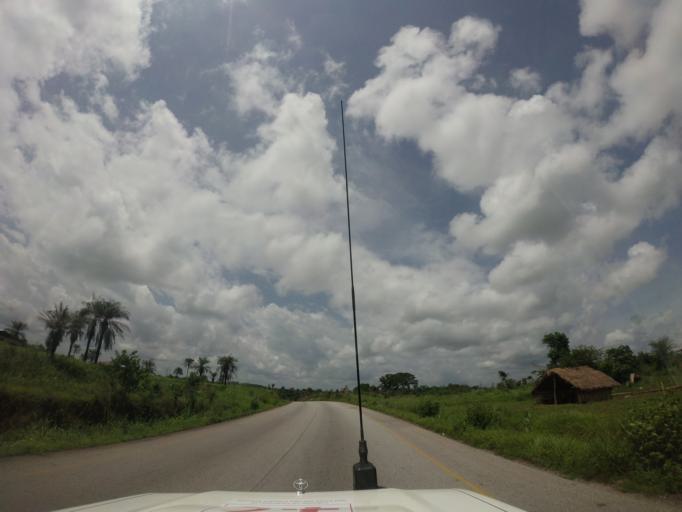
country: SL
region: Northern Province
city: Lunsar
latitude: 8.4579
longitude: -12.5041
